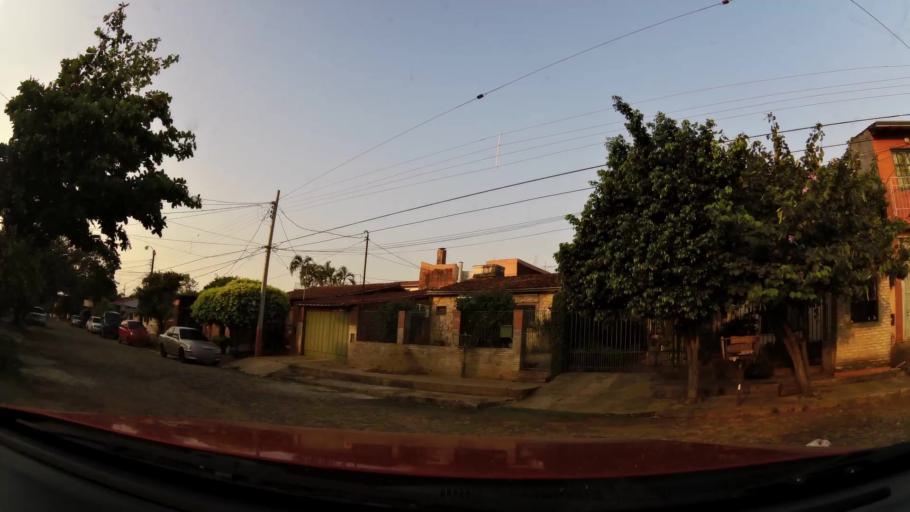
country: PY
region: Central
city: Lambare
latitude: -25.3458
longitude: -57.5996
